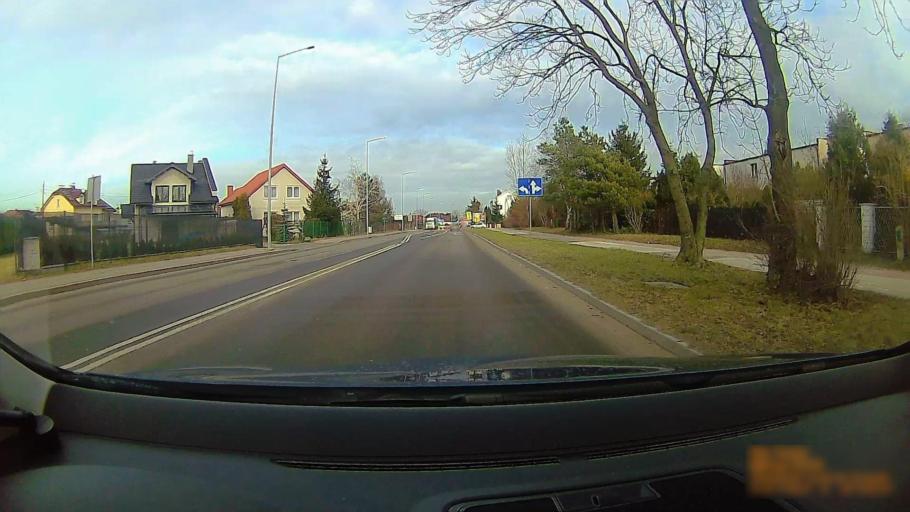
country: PL
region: Greater Poland Voivodeship
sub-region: Konin
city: Konin
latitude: 52.1991
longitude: 18.2423
